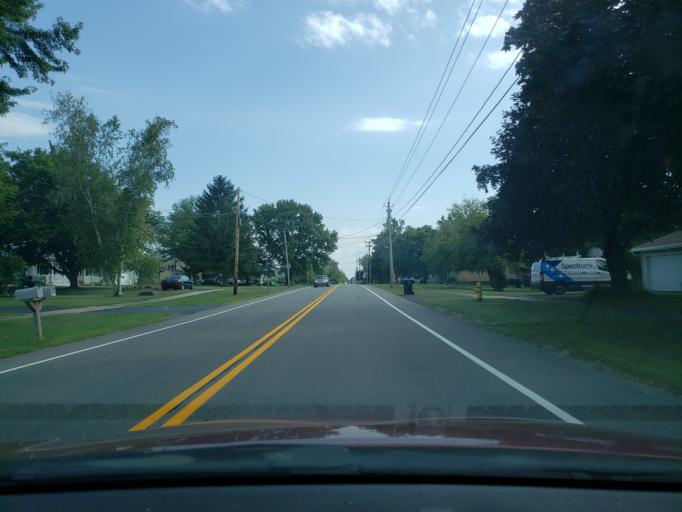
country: US
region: New York
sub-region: Monroe County
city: Greece
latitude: 43.2728
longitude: -77.7150
